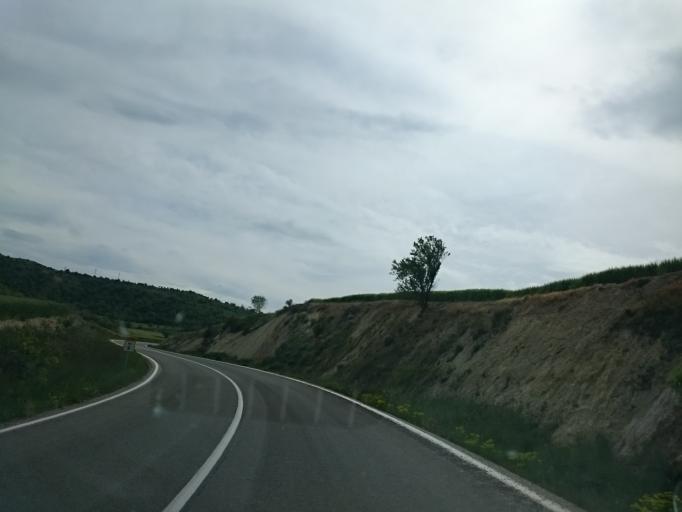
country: ES
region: Catalonia
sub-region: Provincia de Lleida
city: Tora de Riubregos
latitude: 41.7964
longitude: 1.4018
